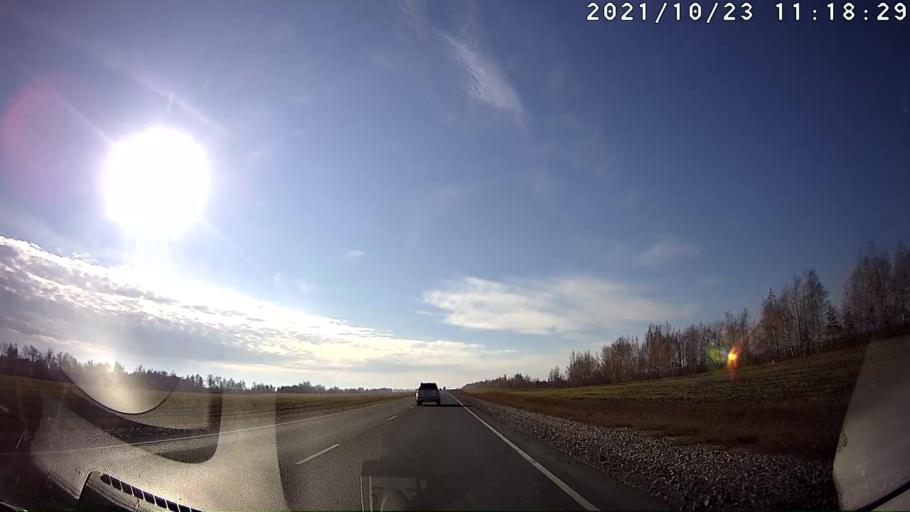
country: RU
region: Saratov
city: Kamenskiy
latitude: 50.8959
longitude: 45.5923
